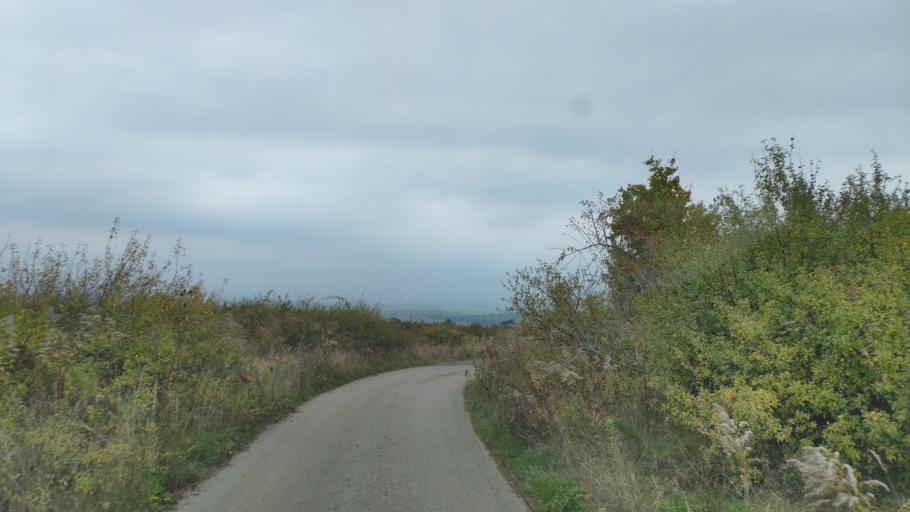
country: SK
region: Kosicky
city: Kosice
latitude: 48.6302
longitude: 21.4009
